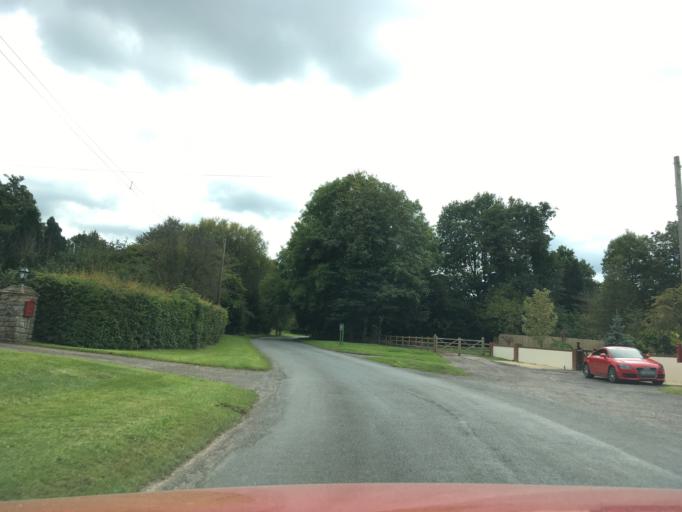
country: GB
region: England
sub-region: Gloucestershire
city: Berkeley
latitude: 51.6703
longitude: -2.4215
